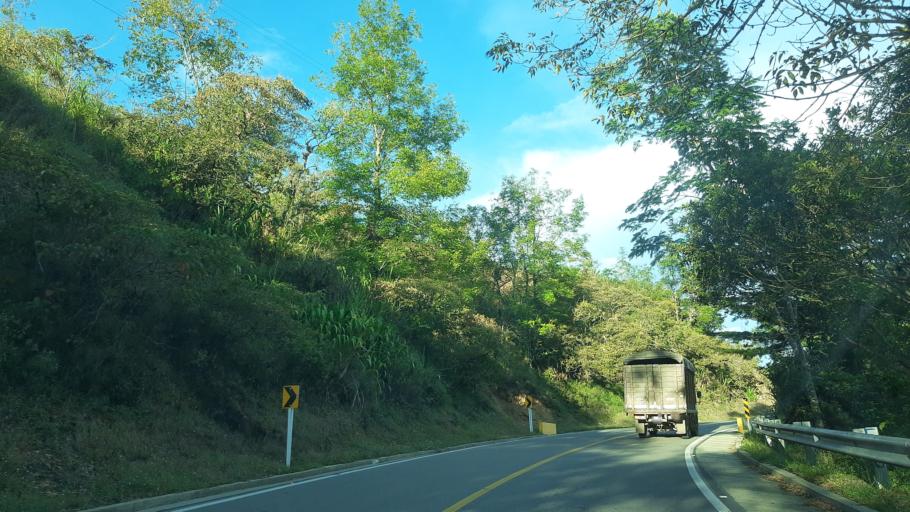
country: CO
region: Boyaca
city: Guateque
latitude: 5.0050
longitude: -73.4978
